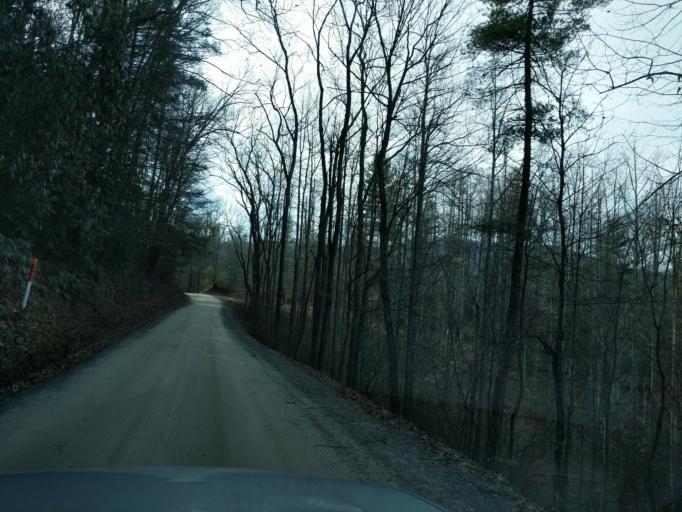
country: US
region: North Carolina
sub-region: Haywood County
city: Cove Creek
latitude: 35.6702
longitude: -83.0253
